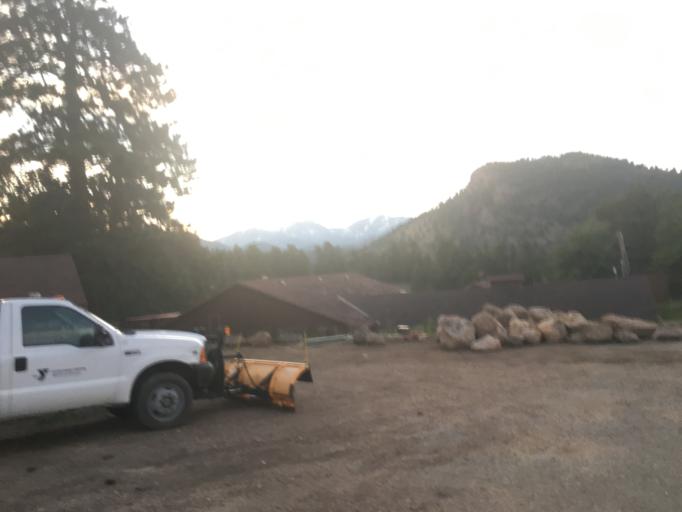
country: US
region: Colorado
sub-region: Larimer County
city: Estes Park
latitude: 40.3434
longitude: -105.5719
